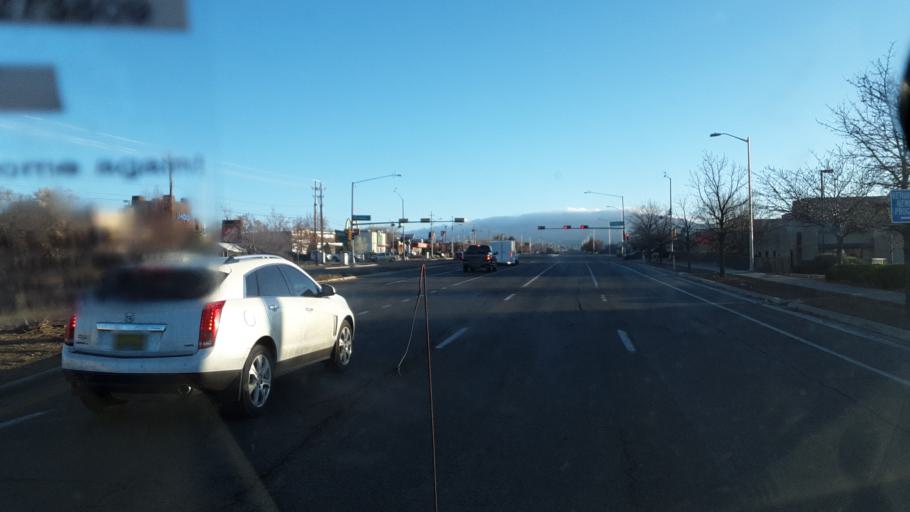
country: US
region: New Mexico
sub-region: Santa Fe County
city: Agua Fria
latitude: 35.6489
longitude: -106.0020
